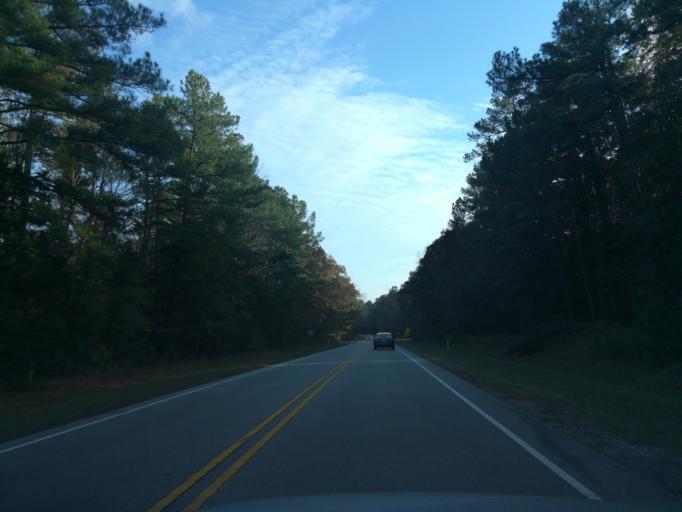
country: US
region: North Carolina
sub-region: Durham County
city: Durham
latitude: 36.0191
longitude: -78.9837
